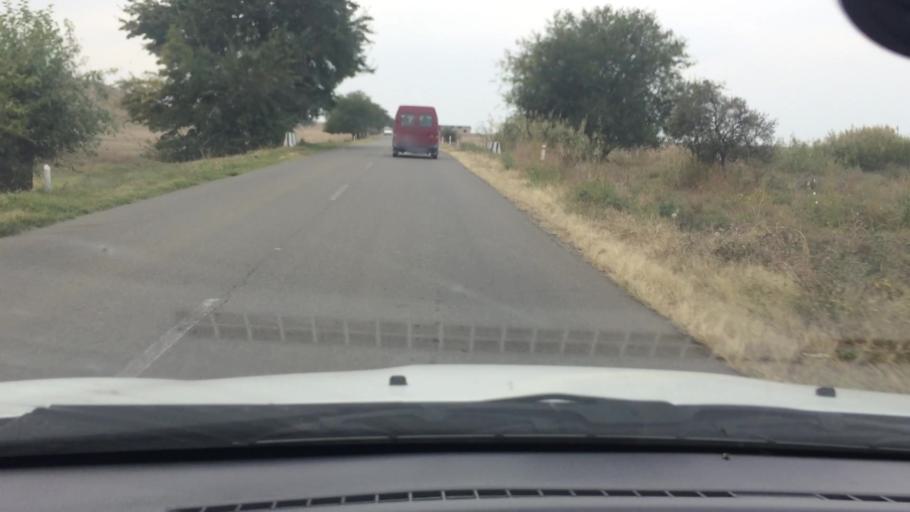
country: AM
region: Tavush
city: Berdavan
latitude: 41.3361
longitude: 45.0206
